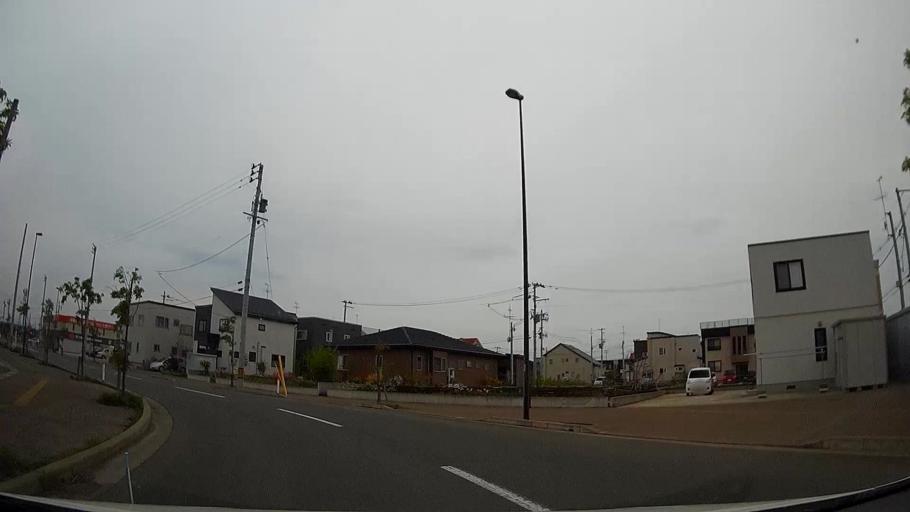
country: JP
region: Aomori
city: Aomori Shi
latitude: 40.8318
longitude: 140.6924
